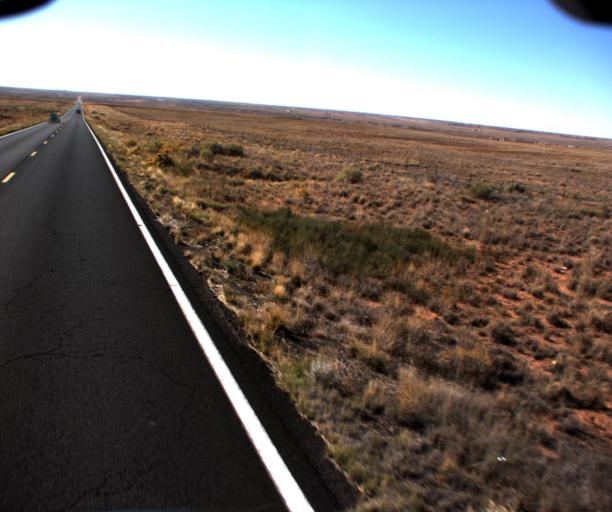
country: US
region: Arizona
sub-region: Navajo County
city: Dilkon
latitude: 35.2727
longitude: -110.4292
